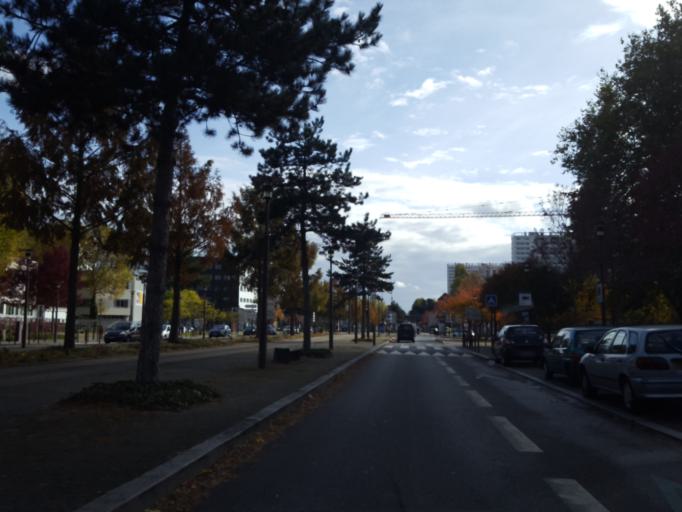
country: FR
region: Pays de la Loire
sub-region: Departement de la Loire-Atlantique
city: Nantes
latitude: 47.2077
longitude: -1.5402
